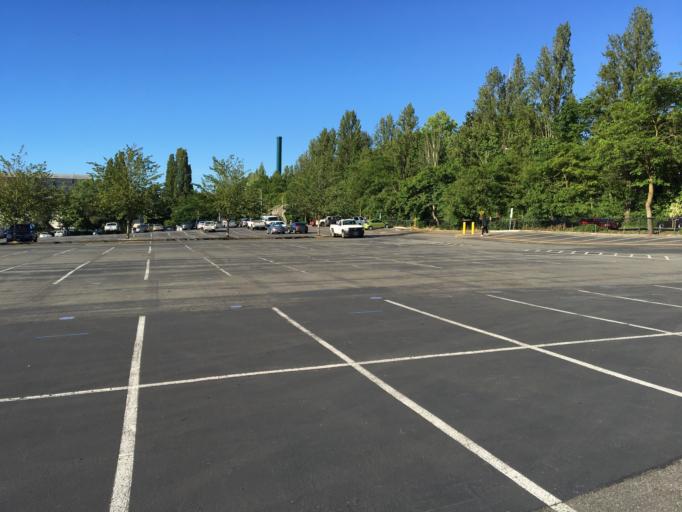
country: US
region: Washington
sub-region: King County
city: Seattle
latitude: 47.6572
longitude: -122.3011
